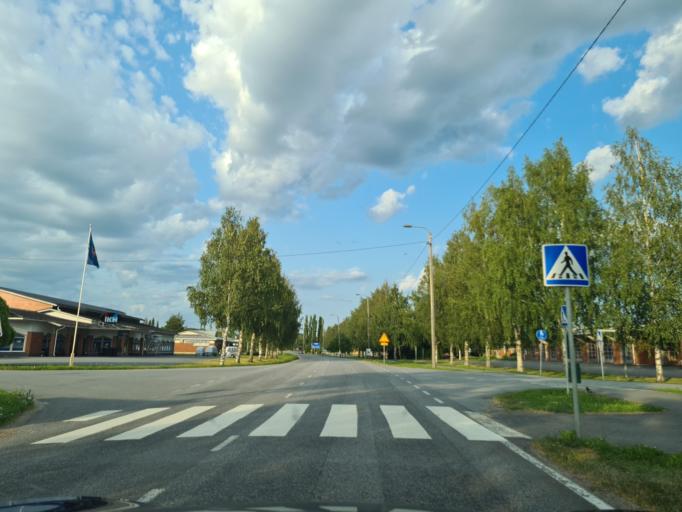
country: FI
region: Southern Ostrobothnia
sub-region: Seinaejoki
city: Lapua
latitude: 62.9748
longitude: 23.0171
